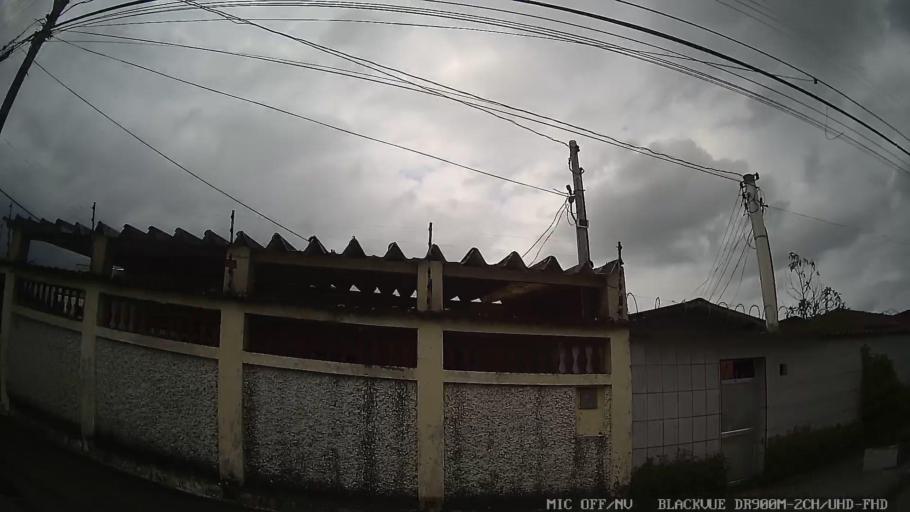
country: BR
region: Sao Paulo
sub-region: Guaruja
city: Guaruja
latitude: -23.9965
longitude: -46.2889
